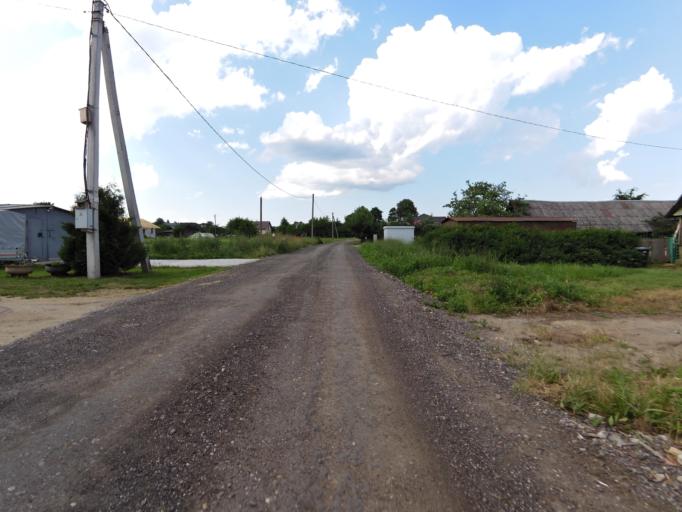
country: LT
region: Vilnius County
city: Pasilaiciai
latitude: 54.7596
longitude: 25.2300
